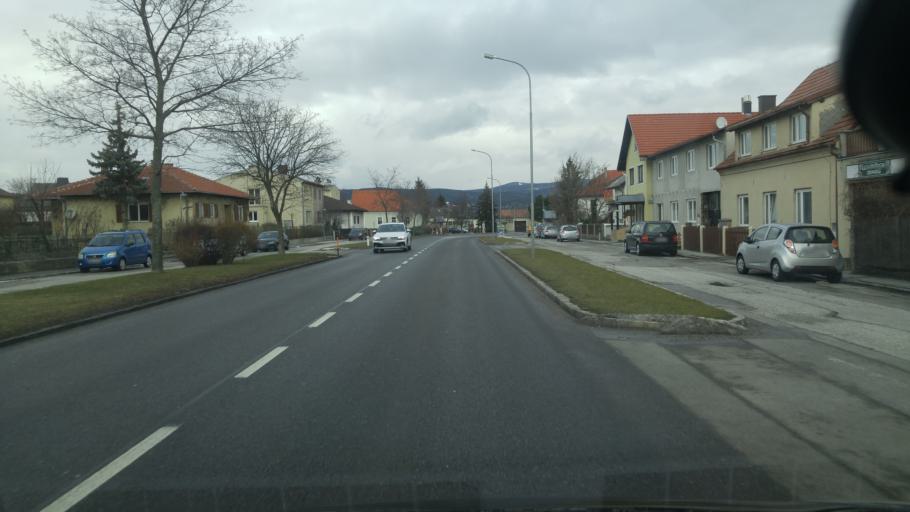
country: AT
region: Lower Austria
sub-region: Politischer Bezirk Baden
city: Bad Voslau
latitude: 47.9827
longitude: 16.2211
